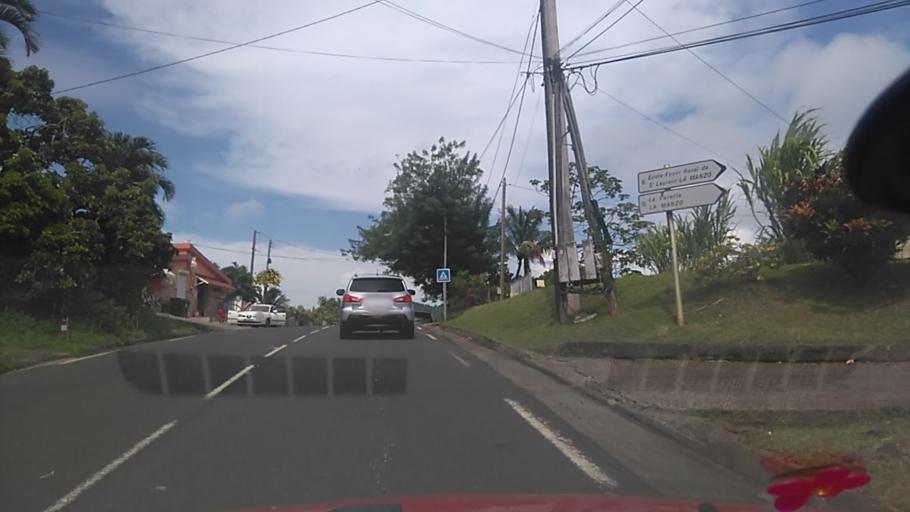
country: MQ
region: Martinique
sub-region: Martinique
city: Le Francois
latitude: 14.5940
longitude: -60.9224
